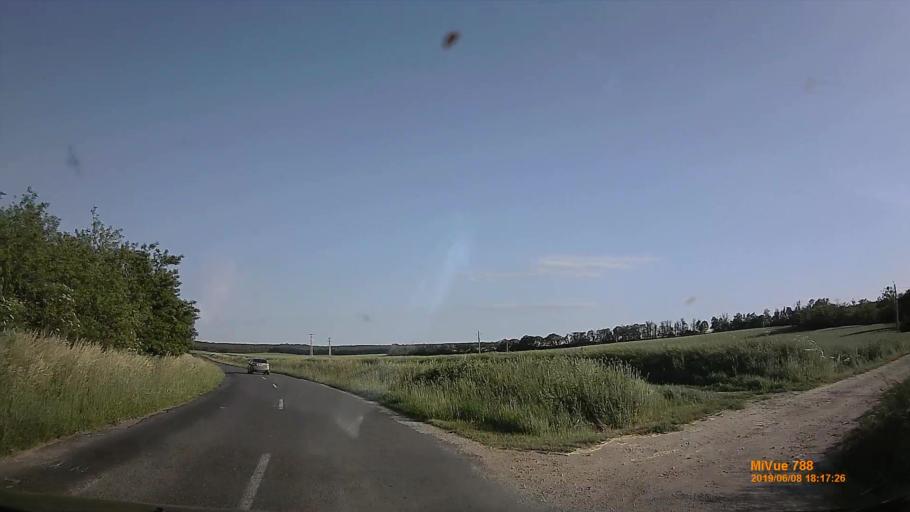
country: HU
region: Vas
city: Csepreg
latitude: 47.3830
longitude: 16.7150
